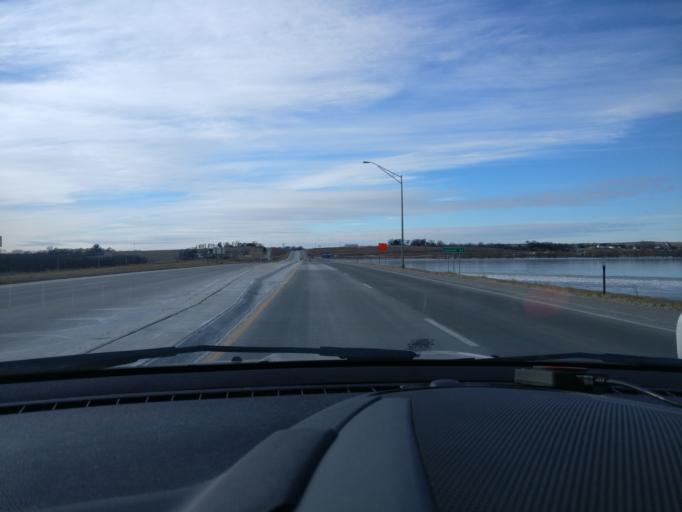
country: US
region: Nebraska
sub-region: Saunders County
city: Wahoo
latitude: 41.2348
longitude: -96.6050
